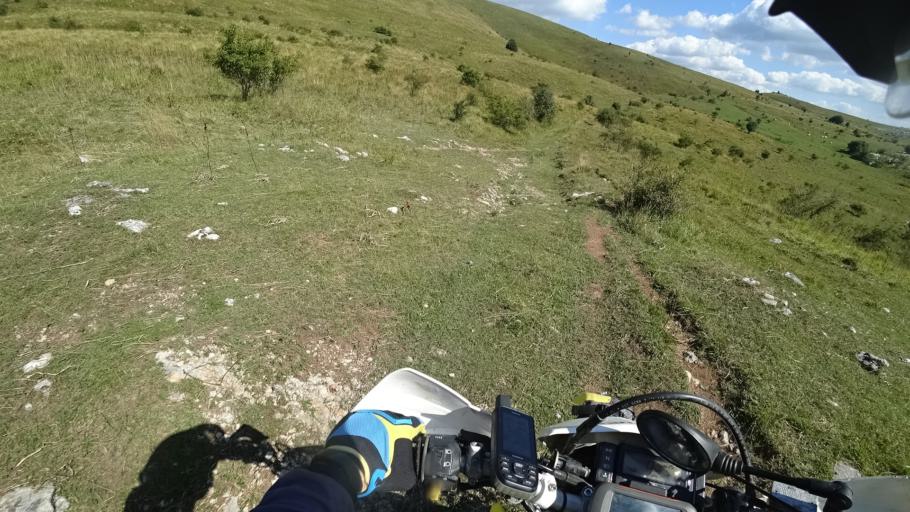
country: HR
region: Zadarska
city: Gracac
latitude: 44.4024
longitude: 16.0076
